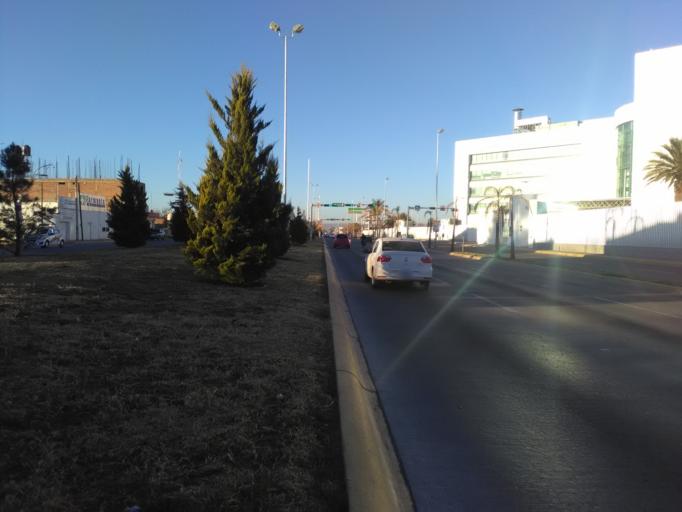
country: MX
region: Durango
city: Victoria de Durango
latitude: 24.0563
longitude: -104.6398
